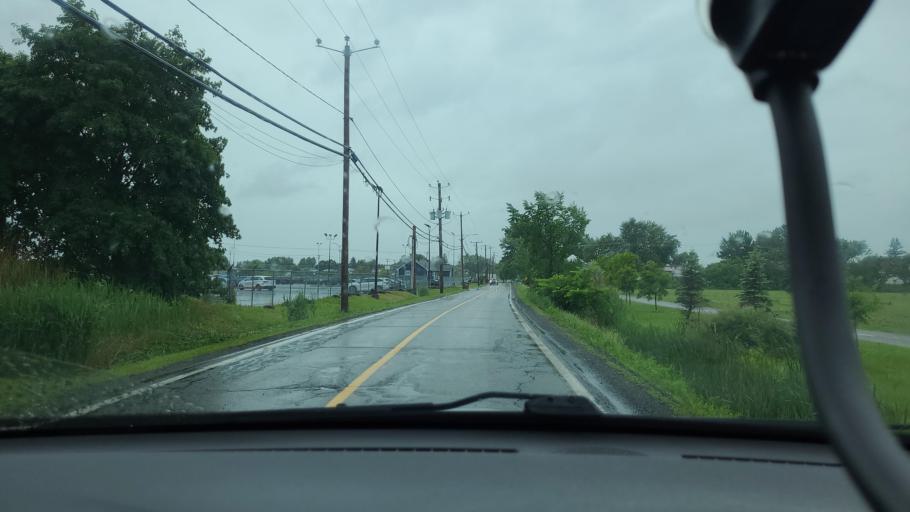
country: CA
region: Quebec
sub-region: Monteregie
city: Saint-Basile-le-Grand
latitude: 45.5330
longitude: -73.2802
